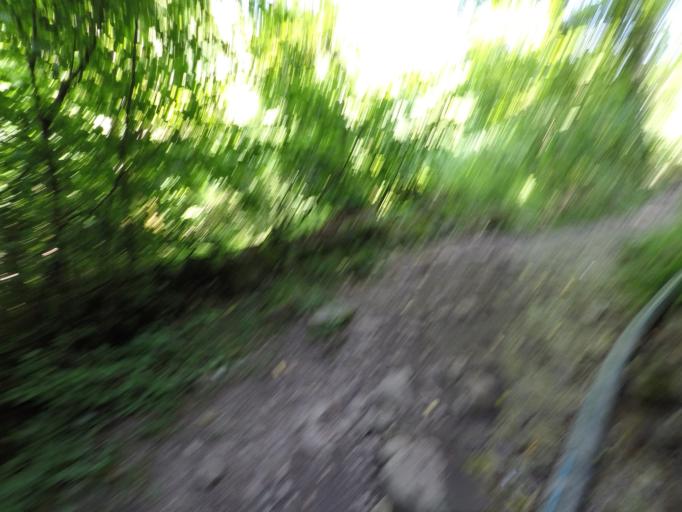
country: AZ
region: Qakh Rayon
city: Cinarli
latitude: 41.4923
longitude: 46.8587
